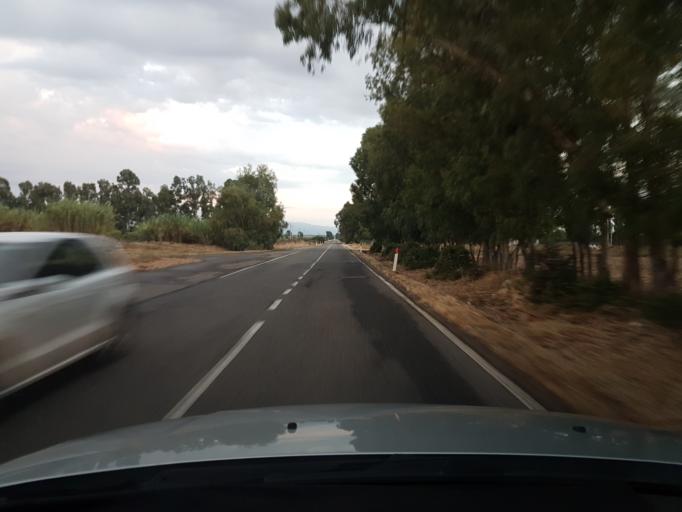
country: IT
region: Sardinia
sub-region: Provincia di Oristano
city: Milis
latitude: 40.0344
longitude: 8.6383
